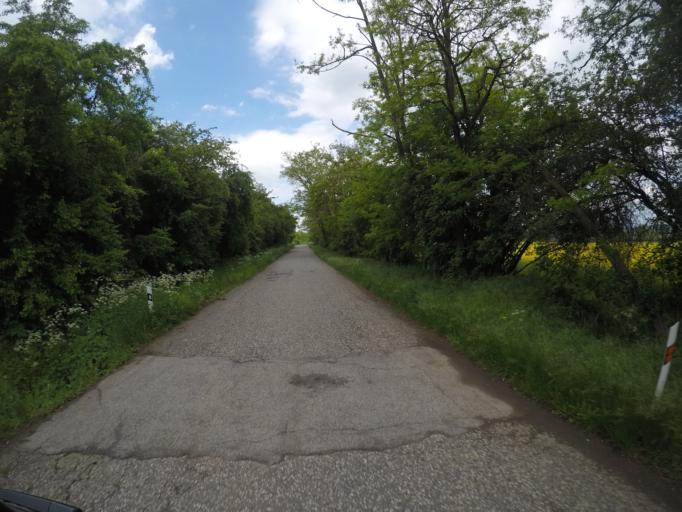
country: SK
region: Banskobystricky
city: Dudince
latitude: 48.0992
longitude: 18.8703
